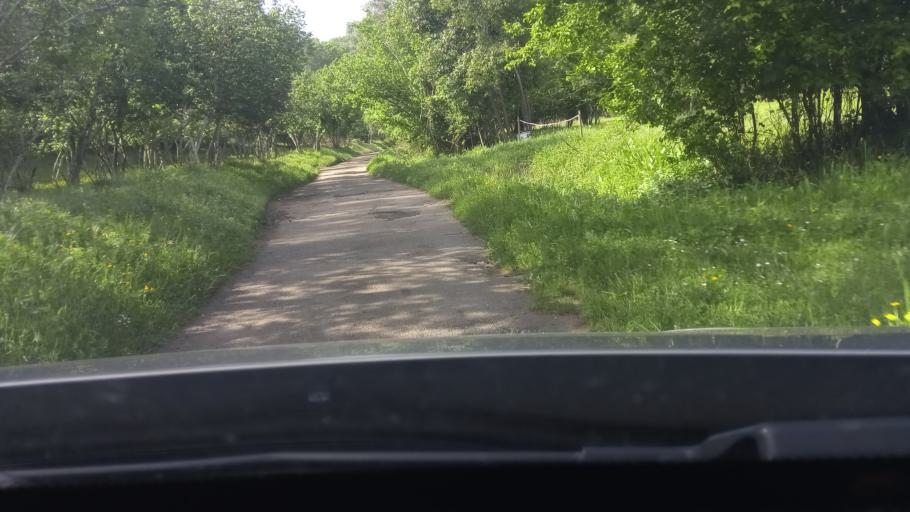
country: IT
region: Latium
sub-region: Provincia di Latina
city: Minturno
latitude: 41.2787
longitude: 13.7660
